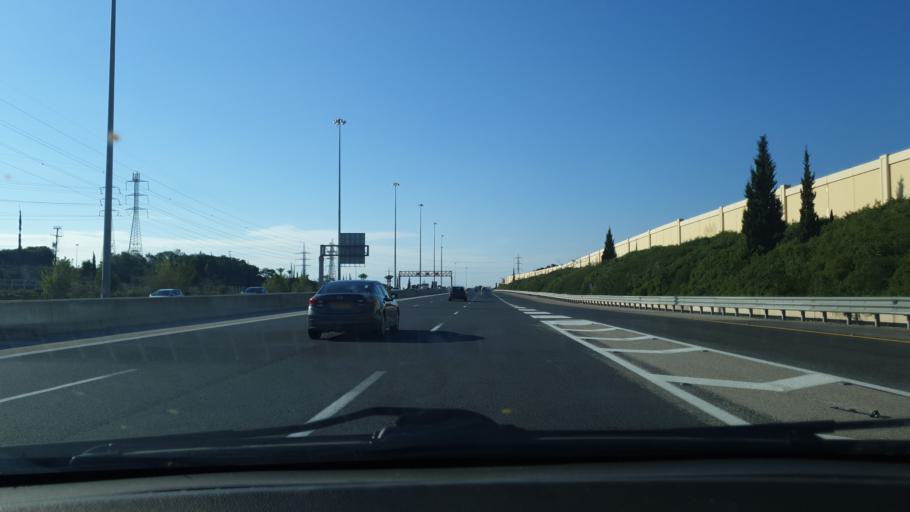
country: IL
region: Central District
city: Rishon LeZiyyon
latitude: 31.9649
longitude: 34.7652
